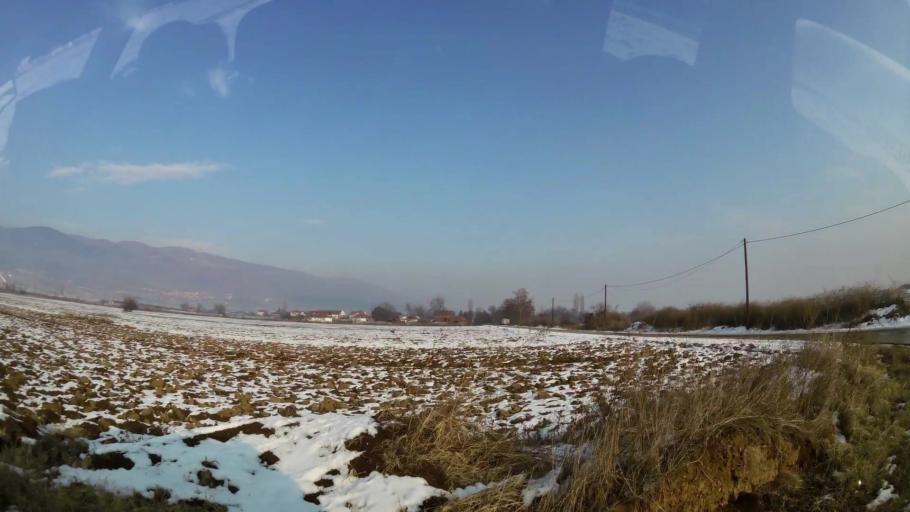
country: MK
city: Creshevo
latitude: 42.0260
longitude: 21.5059
